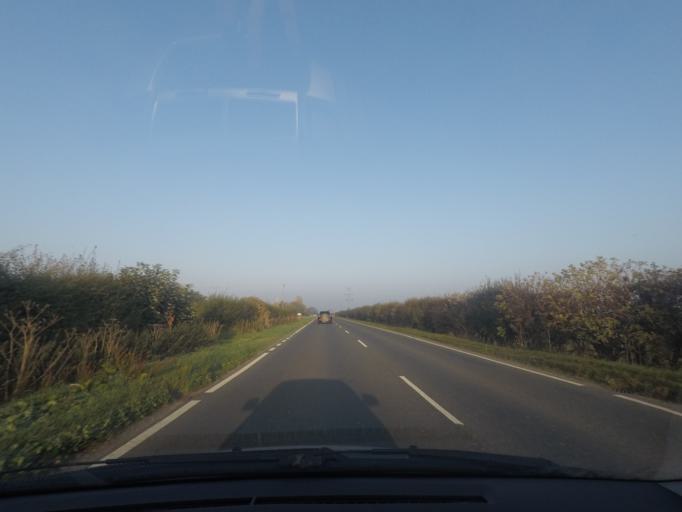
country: GB
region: England
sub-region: City of York
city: Askham Richard
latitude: 53.9901
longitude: -1.2321
